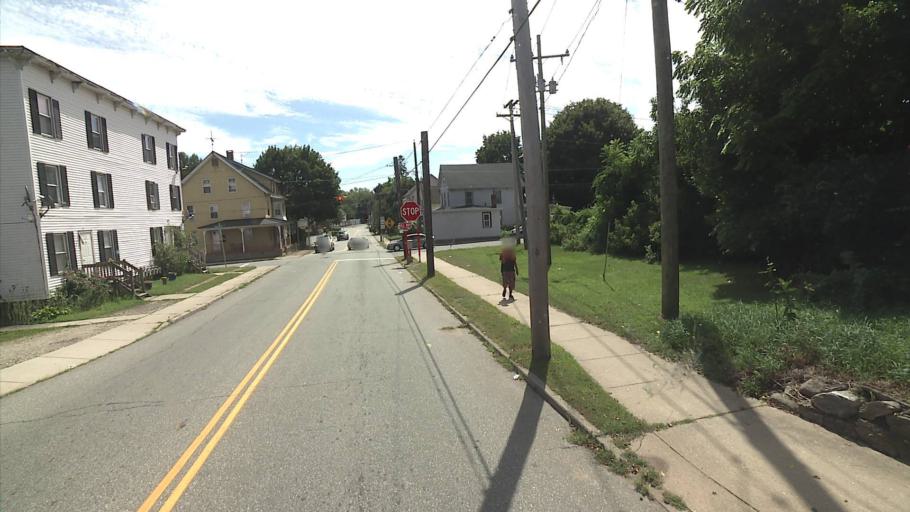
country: US
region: Connecticut
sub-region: Windham County
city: Willimantic
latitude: 41.7172
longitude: -72.1989
